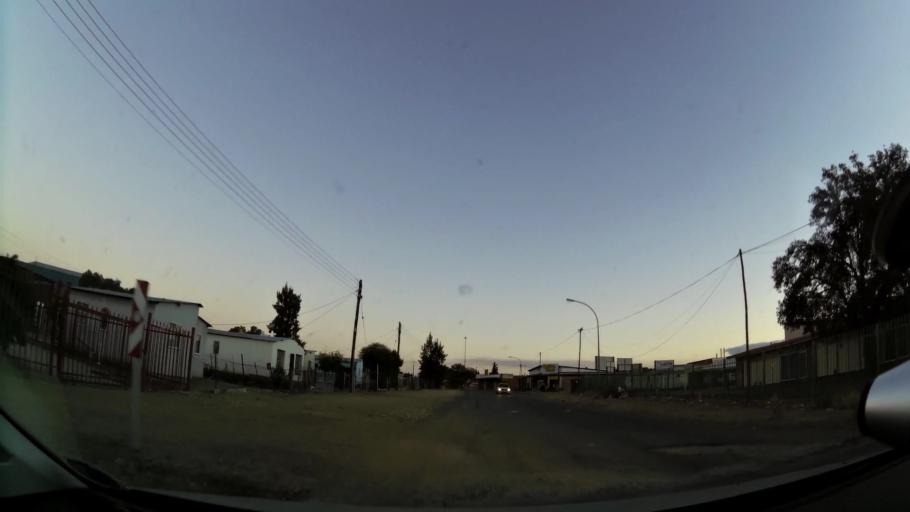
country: ZA
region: Northern Cape
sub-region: Frances Baard District Municipality
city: Kimberley
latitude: -28.7172
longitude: 24.7674
